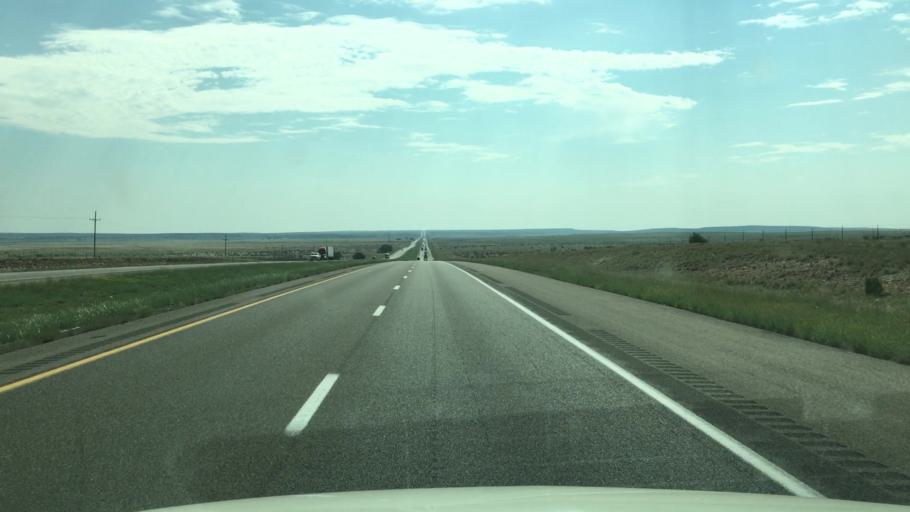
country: US
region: New Mexico
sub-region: Guadalupe County
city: Santa Rosa
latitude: 34.9793
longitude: -105.0514
